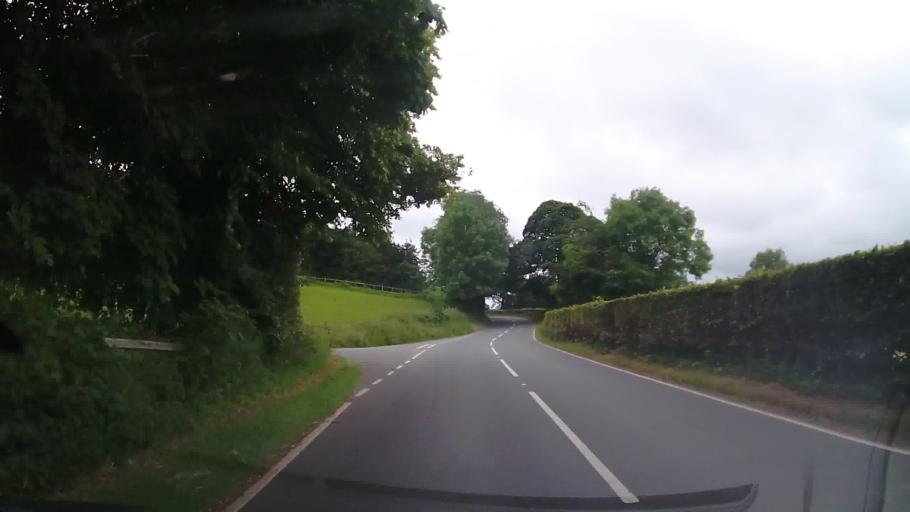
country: GB
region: Wales
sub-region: Denbighshire
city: Llandrillo
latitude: 52.9472
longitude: -3.4163
